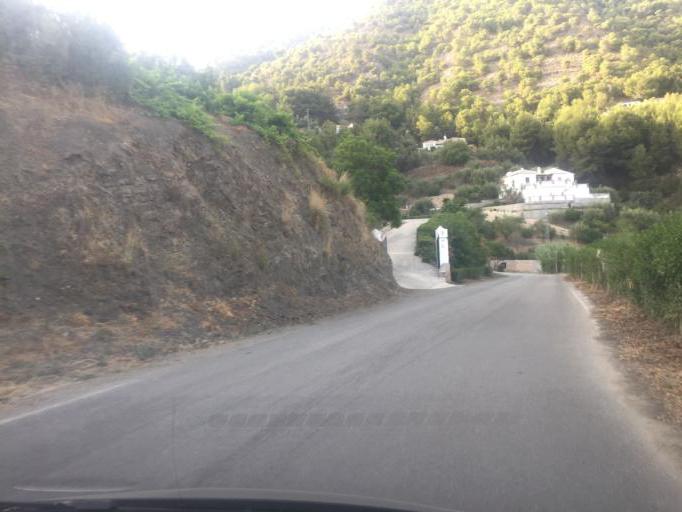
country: ES
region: Andalusia
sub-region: Provincia de Malaga
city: Frigiliana
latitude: 36.8043
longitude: -3.9173
